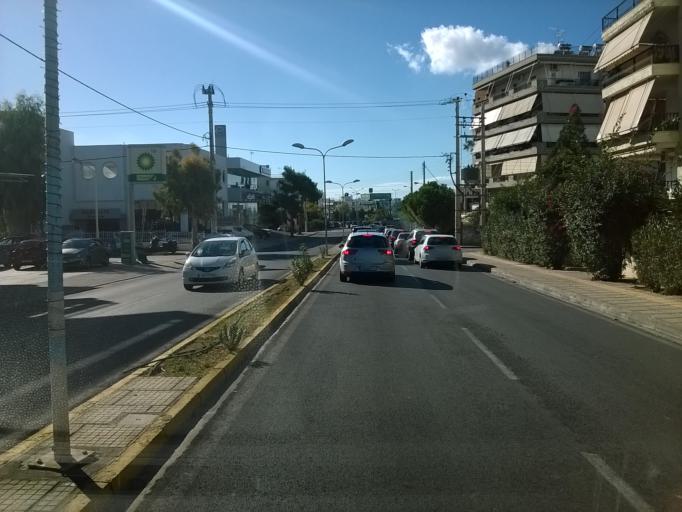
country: GR
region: Attica
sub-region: Nomarchia Athinas
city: Glyfada
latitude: 37.8769
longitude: 23.7576
